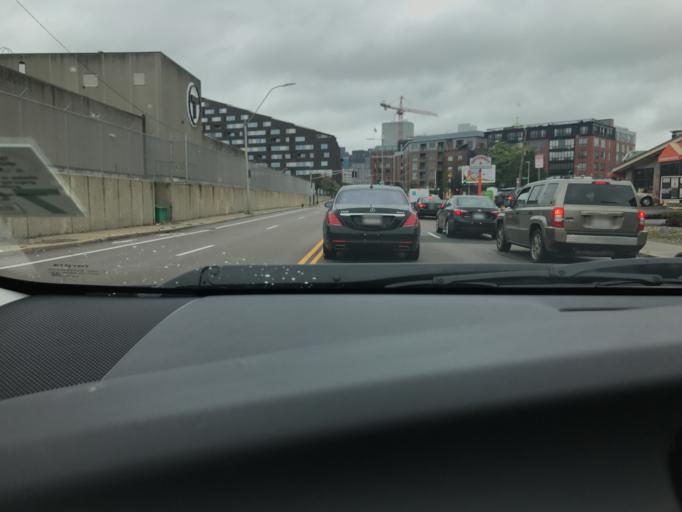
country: US
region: Massachusetts
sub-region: Suffolk County
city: South Boston
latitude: 42.3397
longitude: -71.0571
